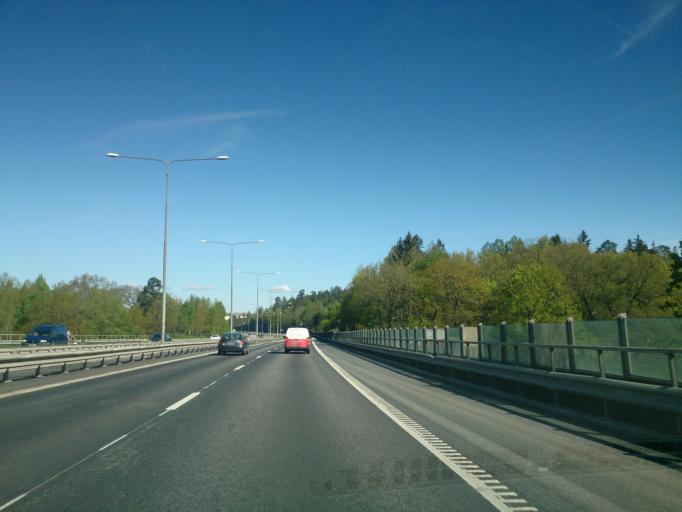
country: SE
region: Stockholm
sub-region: Haninge Kommun
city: Handen
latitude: 59.2341
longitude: 18.1234
